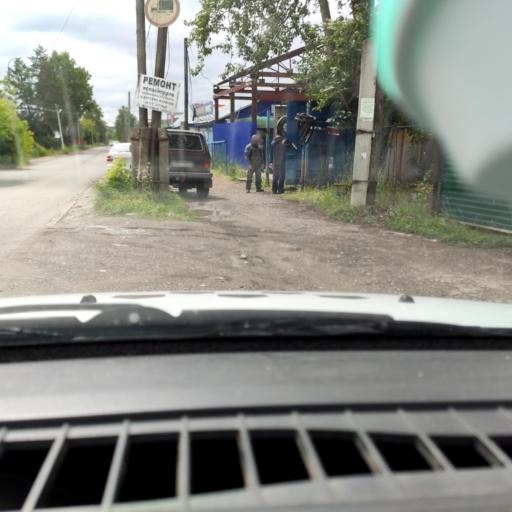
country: RU
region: Perm
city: Dobryanka
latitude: 58.4674
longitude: 56.4095
